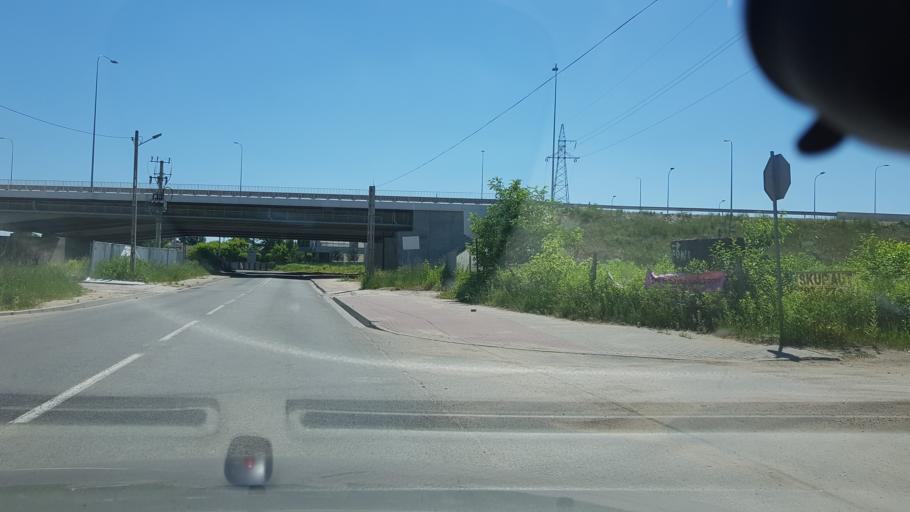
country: PL
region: Masovian Voivodeship
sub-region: Powiat wolominski
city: Marki
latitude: 52.3133
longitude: 21.1247
